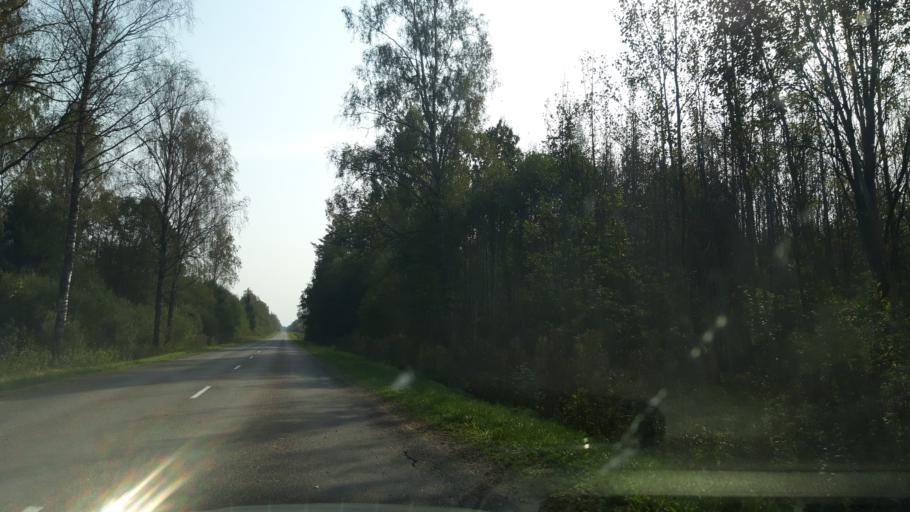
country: LV
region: Burtnieki
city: Matisi
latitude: 57.6524
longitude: 25.2343
